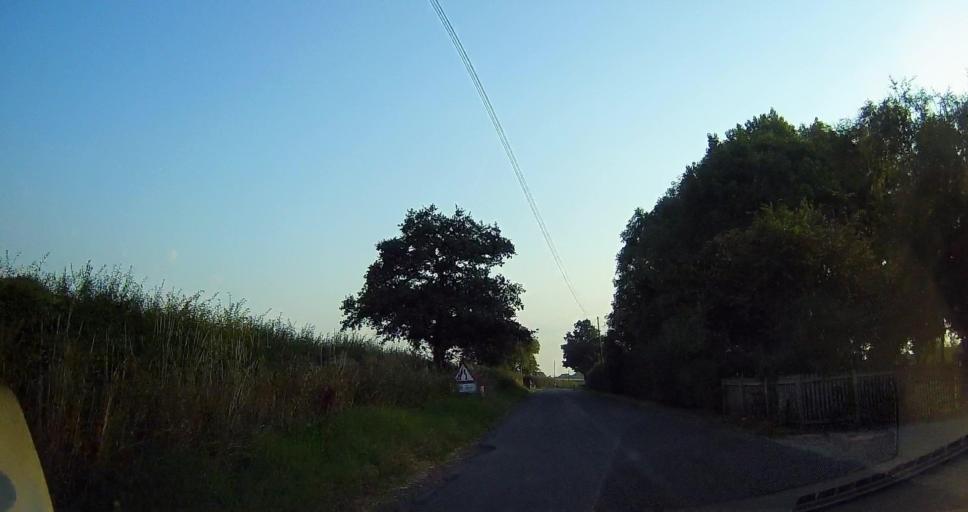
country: GB
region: England
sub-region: Cheshire East
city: Nantwich
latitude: 53.0050
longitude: -2.5293
